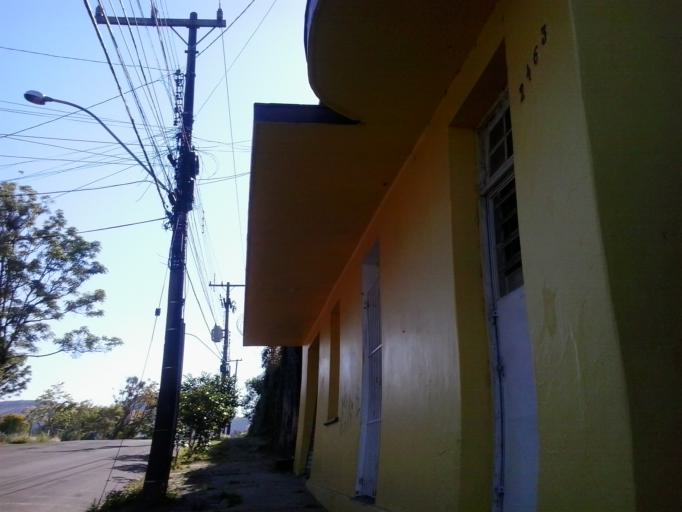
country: BR
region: Rio Grande do Sul
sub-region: Santa Maria
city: Santa Maria
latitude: -29.6818
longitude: -53.8017
